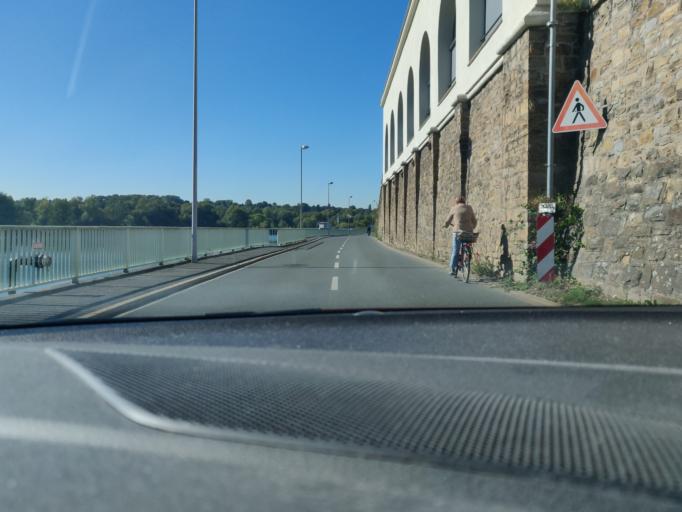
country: DE
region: North Rhine-Westphalia
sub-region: Regierungsbezirk Dusseldorf
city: Muelheim (Ruhr)
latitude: 51.4127
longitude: 6.8821
